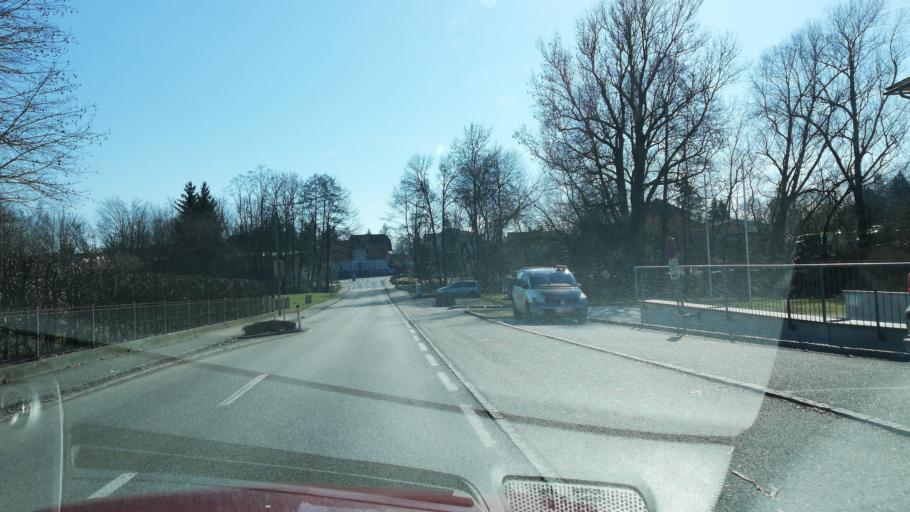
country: AT
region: Upper Austria
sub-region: Politischer Bezirk Vocklabruck
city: Schwanenstadt
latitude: 48.0591
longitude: 13.7792
